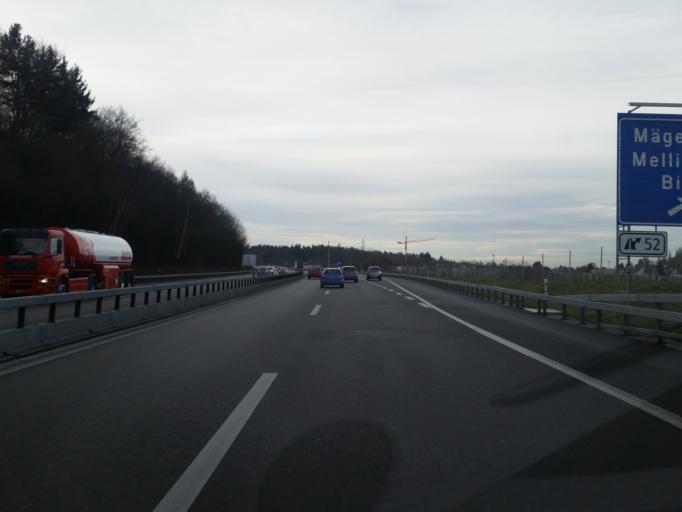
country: CH
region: Aargau
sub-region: Bezirk Lenzburg
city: Othmarsingen
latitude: 47.4225
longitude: 8.2290
